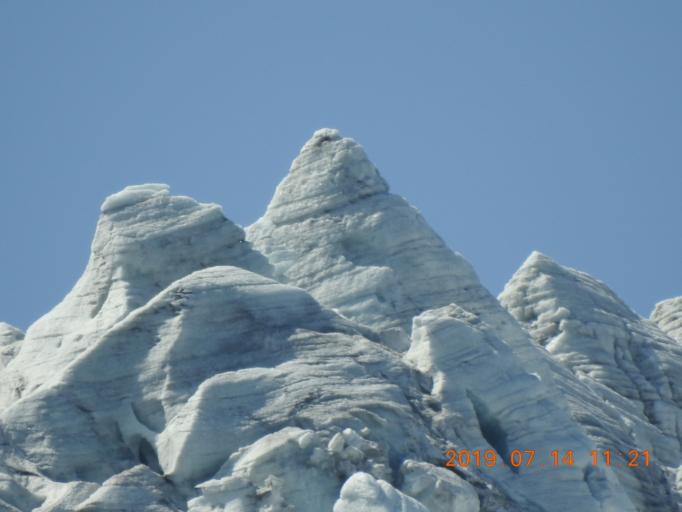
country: NO
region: Hordaland
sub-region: Odda
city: Odda
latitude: 60.0424
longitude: 6.4401
